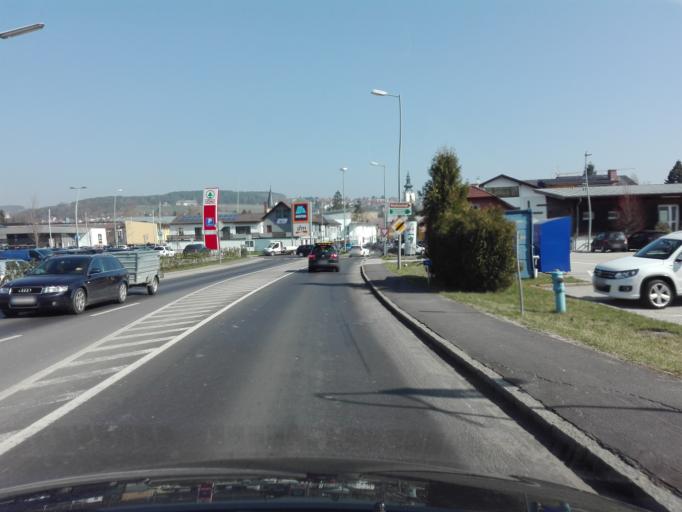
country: AT
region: Upper Austria
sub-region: Politischer Bezirk Urfahr-Umgebung
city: Gallneukirchen
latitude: 48.3498
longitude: 14.4112
